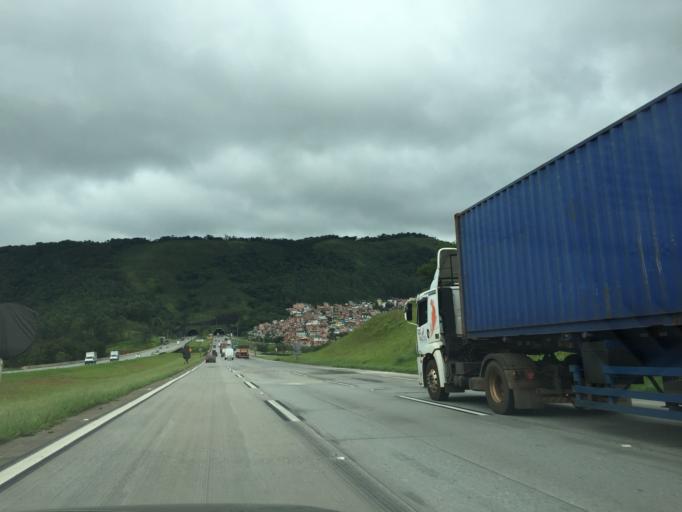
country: BR
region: Sao Paulo
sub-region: Osasco
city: Osasco
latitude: -23.4493
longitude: -46.7835
